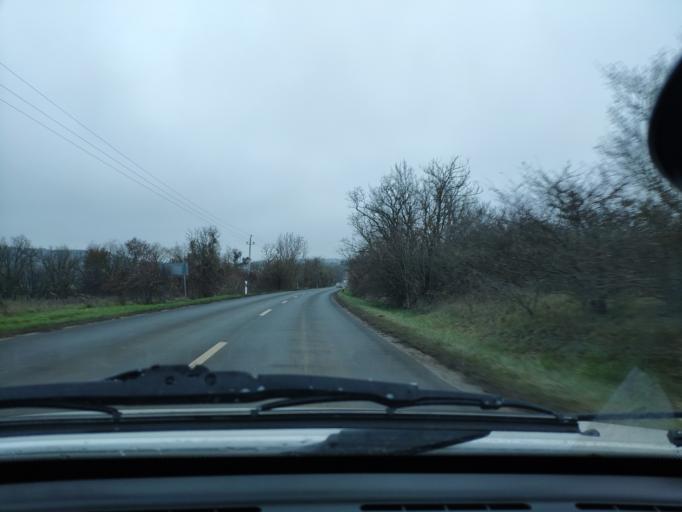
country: HU
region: Pest
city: Soskut
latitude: 47.4191
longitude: 18.8261
